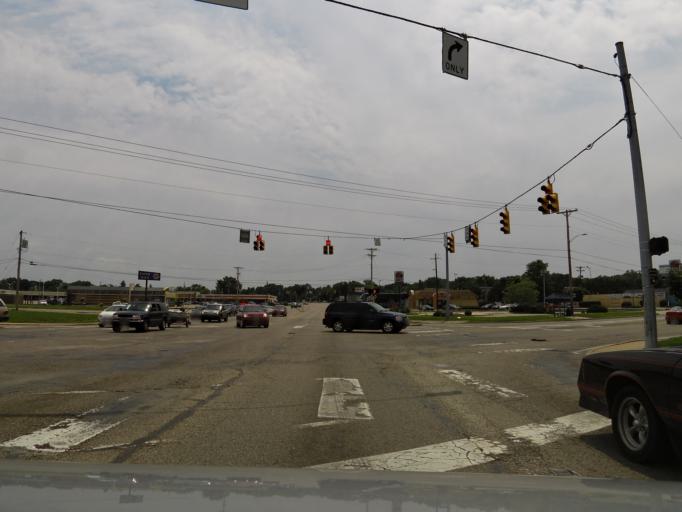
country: US
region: Ohio
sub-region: Montgomery County
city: Riverside
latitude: 39.7694
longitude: -84.1233
